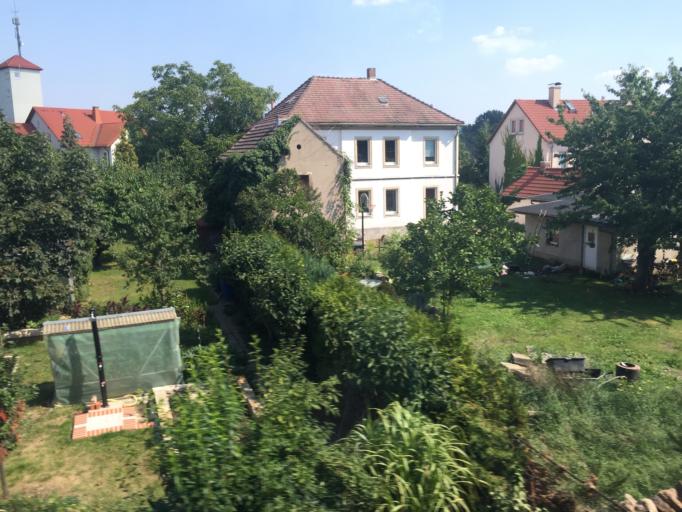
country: DE
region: Saxony
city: Coswig
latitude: 51.1262
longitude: 13.5746
